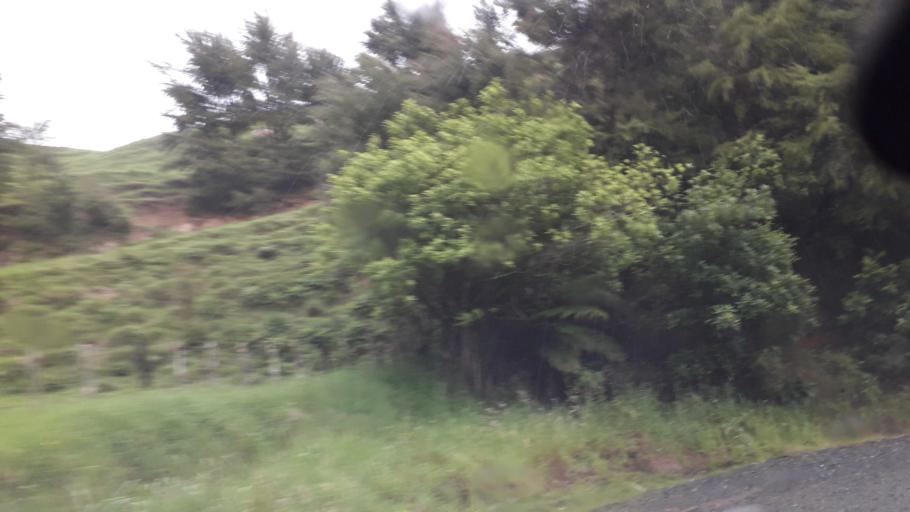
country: NZ
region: Northland
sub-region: Far North District
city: Waimate North
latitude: -35.1445
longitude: 173.7146
